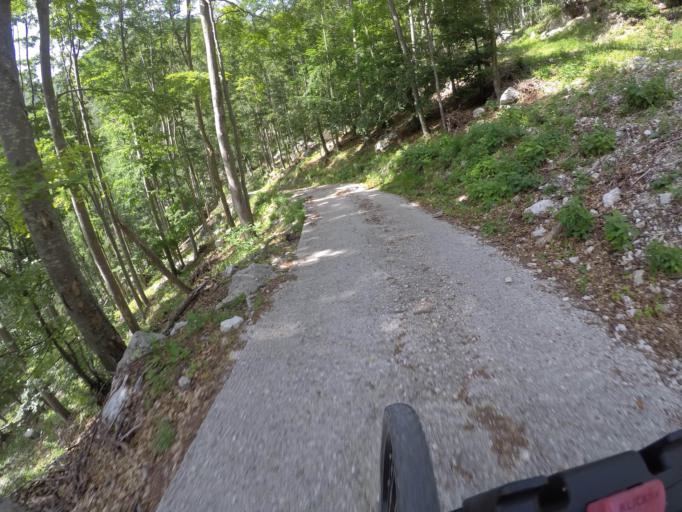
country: IT
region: Friuli Venezia Giulia
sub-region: Provincia di Udine
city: Lusevera
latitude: 46.3134
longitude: 13.2411
